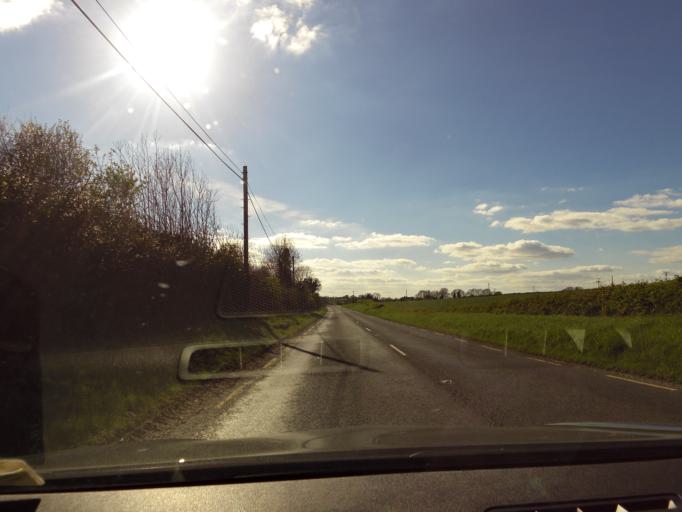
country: IE
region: Leinster
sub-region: Uibh Fhaili
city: Banagher
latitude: 53.1018
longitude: -8.0018
